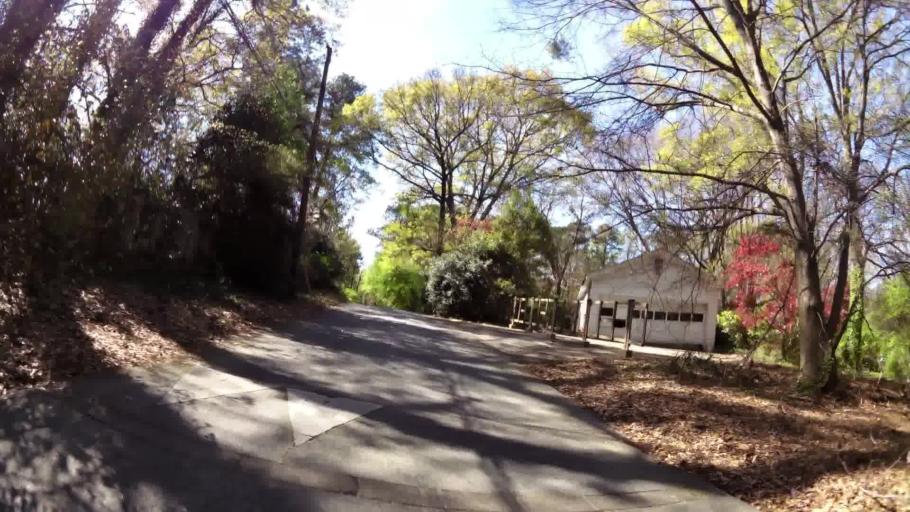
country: US
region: Georgia
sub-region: DeKalb County
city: Clarkston
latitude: 33.8329
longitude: -84.2571
